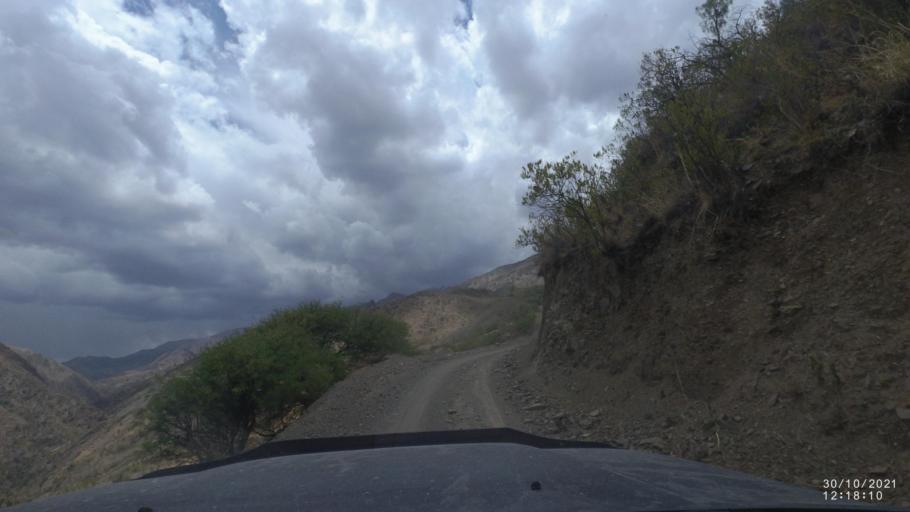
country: BO
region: Cochabamba
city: Colchani
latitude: -17.5671
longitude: -66.6288
